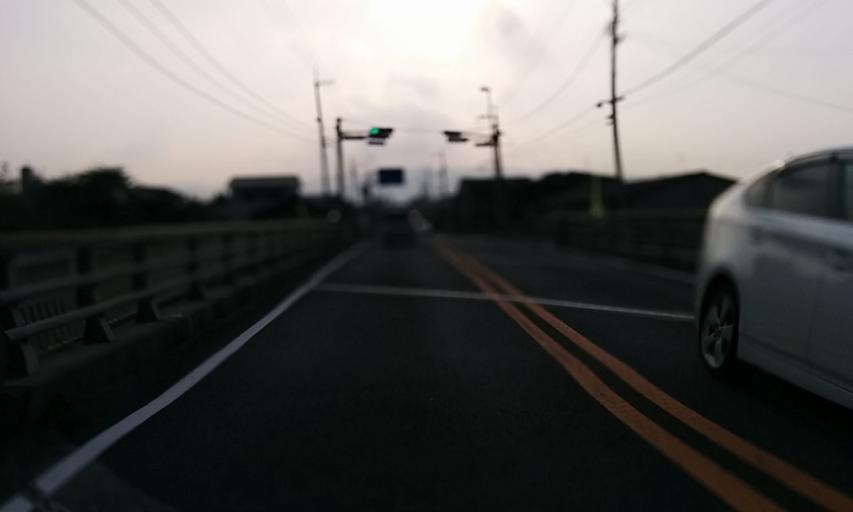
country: JP
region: Ehime
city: Saijo
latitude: 33.8952
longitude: 133.1369
